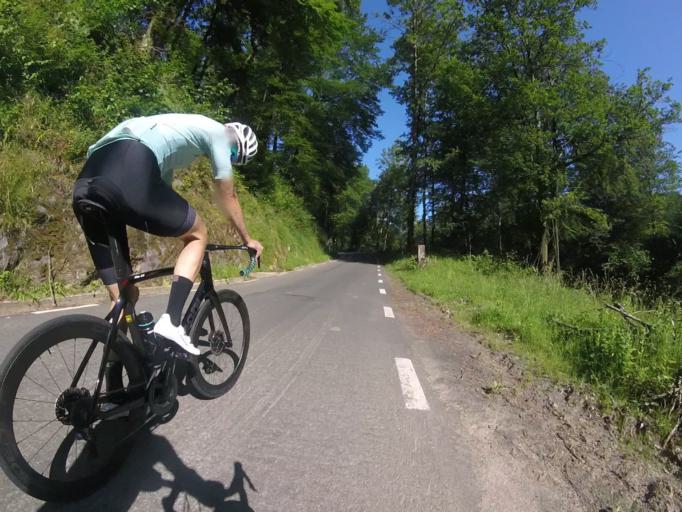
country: ES
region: Basque Country
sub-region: Provincia de Guipuzcoa
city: Beizama
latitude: 43.1385
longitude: -2.2182
